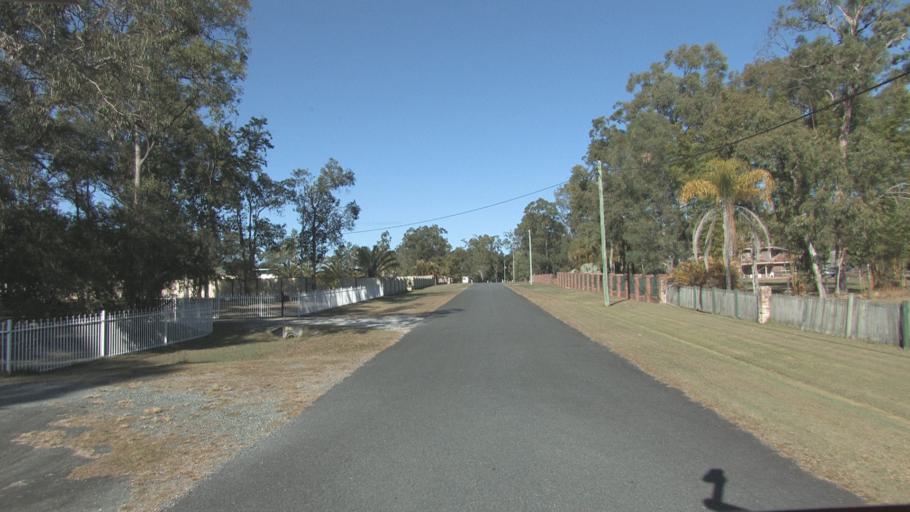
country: AU
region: Queensland
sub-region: Logan
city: Chambers Flat
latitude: -27.7497
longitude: 153.0511
